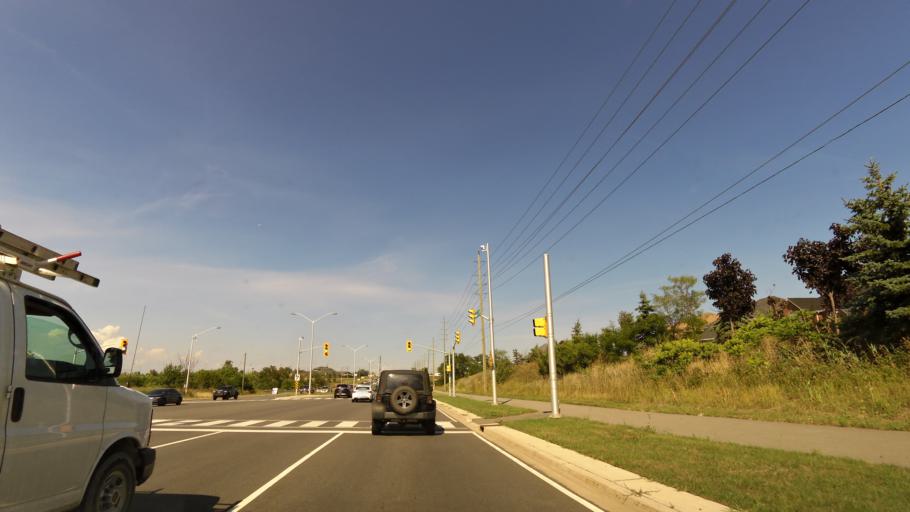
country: CA
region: Ontario
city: Oakville
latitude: 43.5042
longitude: -79.7016
